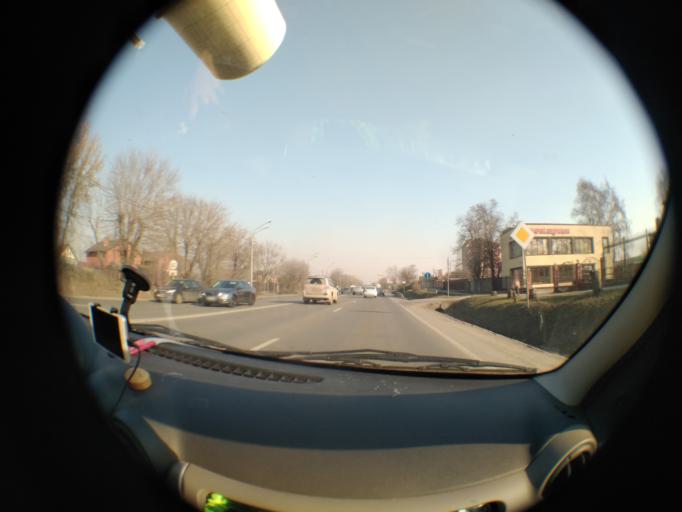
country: RU
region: Moskovskaya
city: Ostrovtsy
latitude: 55.5947
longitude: 37.9933
